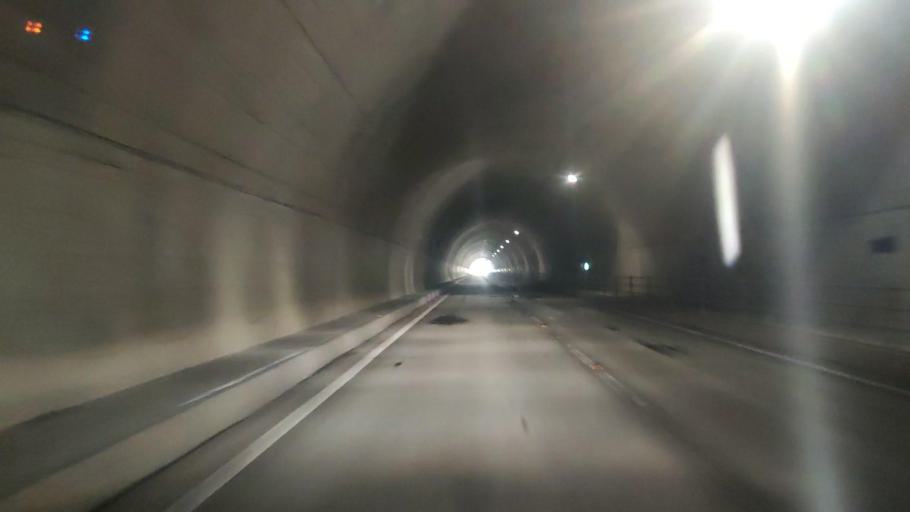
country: JP
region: Miyazaki
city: Nobeoka
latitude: 32.7352
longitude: 131.8251
